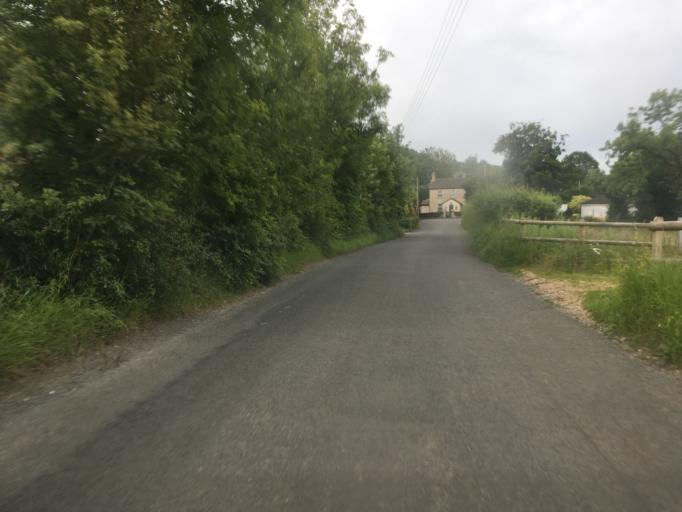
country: GB
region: England
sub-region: North Somerset
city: Dundry
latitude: 51.4058
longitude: -2.6376
